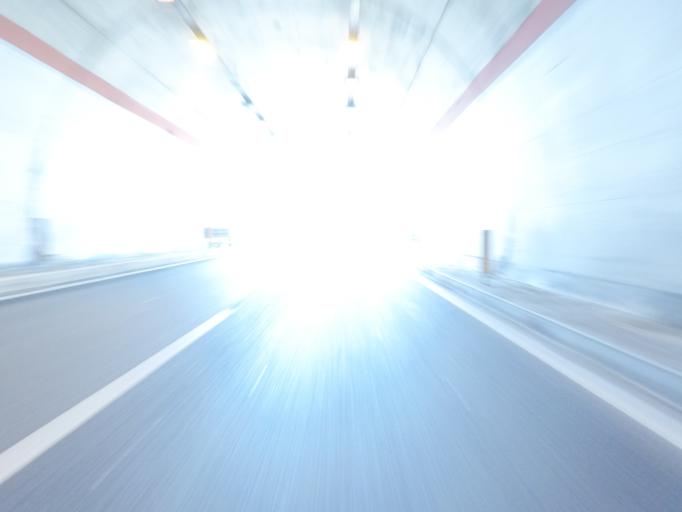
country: IT
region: Tuscany
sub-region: Provincia di Siena
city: Isola D'Arbia
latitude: 43.2740
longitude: 11.3330
